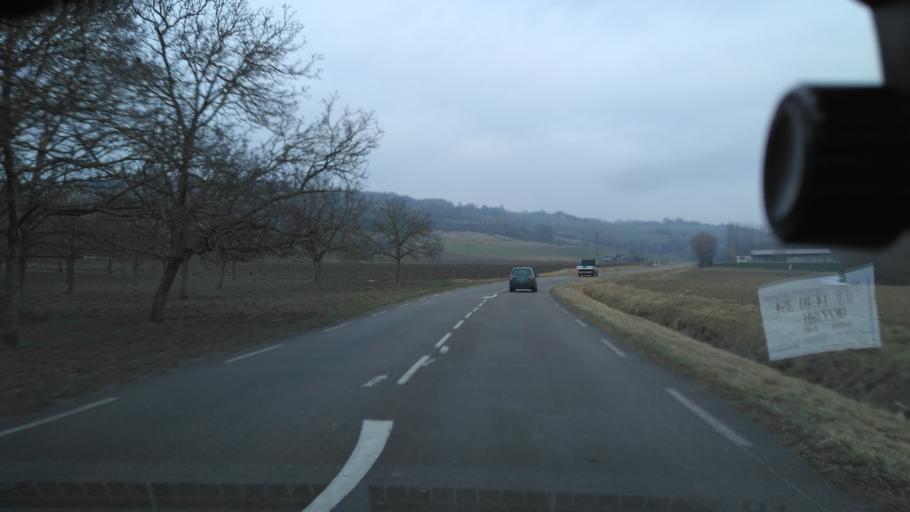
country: FR
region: Rhone-Alpes
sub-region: Departement de la Drome
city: Genissieux
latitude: 45.1476
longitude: 5.1245
